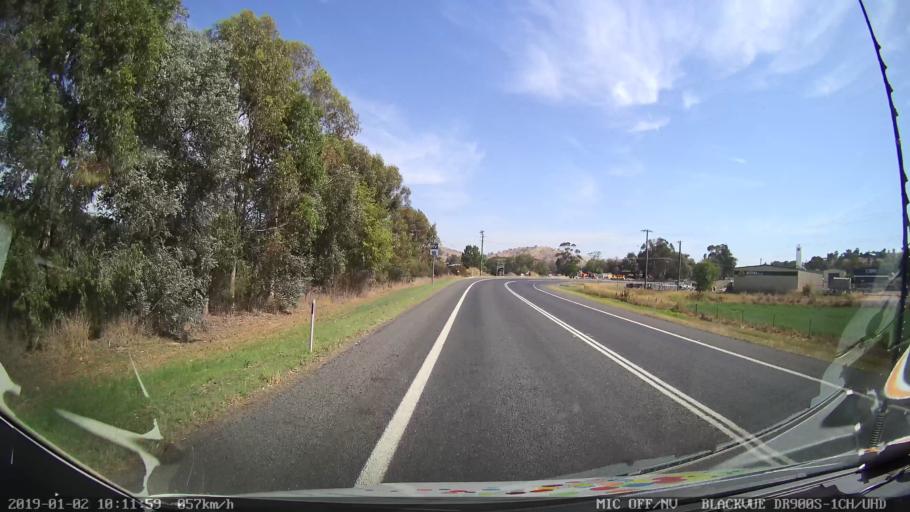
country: AU
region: New South Wales
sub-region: Gundagai
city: Gundagai
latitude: -35.0880
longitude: 148.0938
